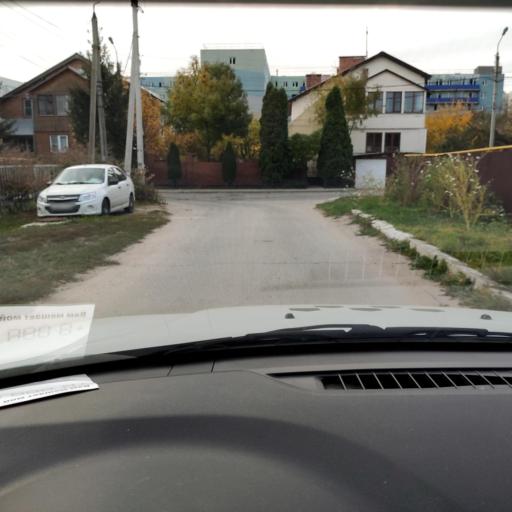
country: RU
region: Samara
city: Tol'yatti
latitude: 53.5334
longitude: 49.3909
